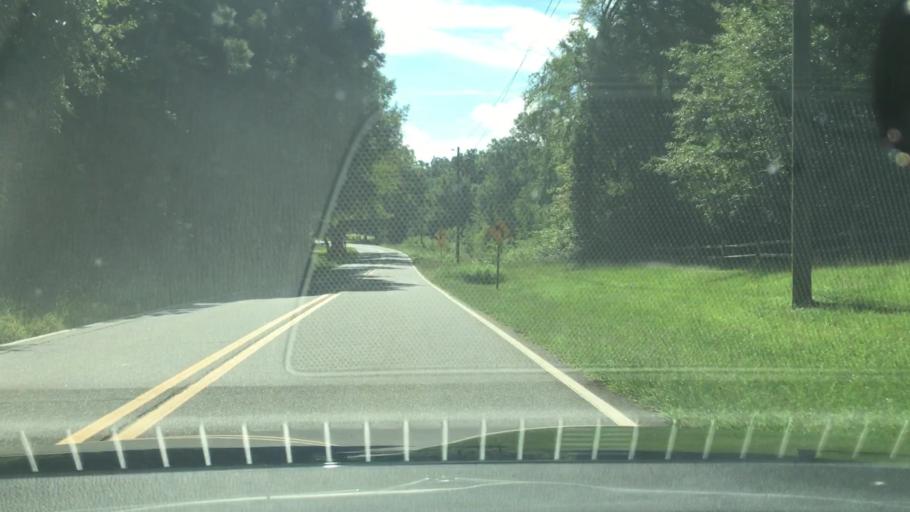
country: US
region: Georgia
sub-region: Putnam County
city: Jefferson
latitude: 33.4387
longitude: -83.3357
